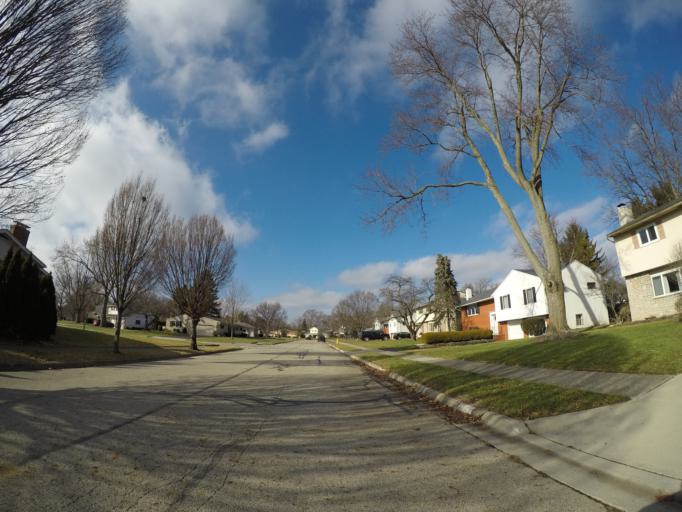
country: US
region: Ohio
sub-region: Franklin County
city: Upper Arlington
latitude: 40.0246
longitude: -83.0603
